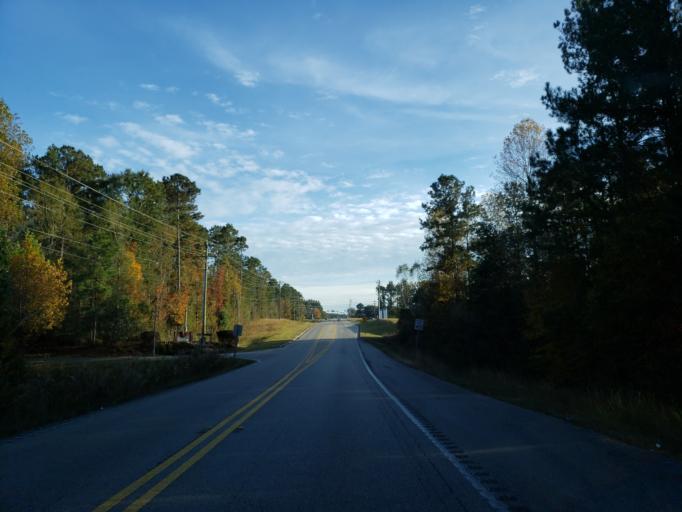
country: US
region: Mississippi
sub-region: Lamar County
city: West Hattiesburg
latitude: 31.2874
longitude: -89.4698
